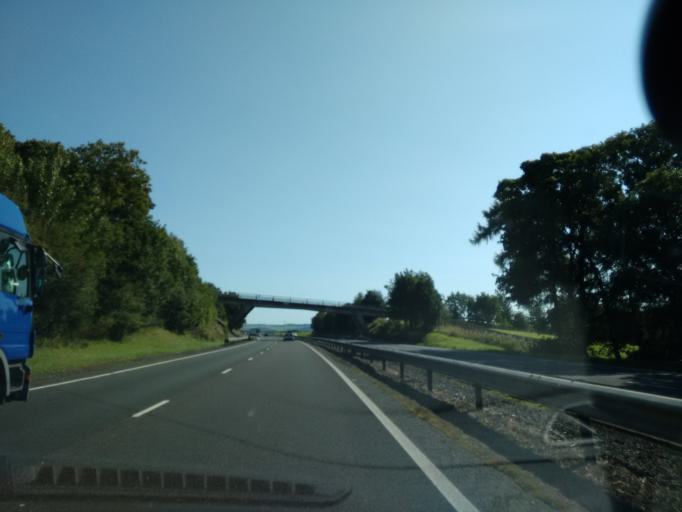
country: GB
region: England
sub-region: Northumberland
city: Corbridge
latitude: 54.9751
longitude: -1.9849
